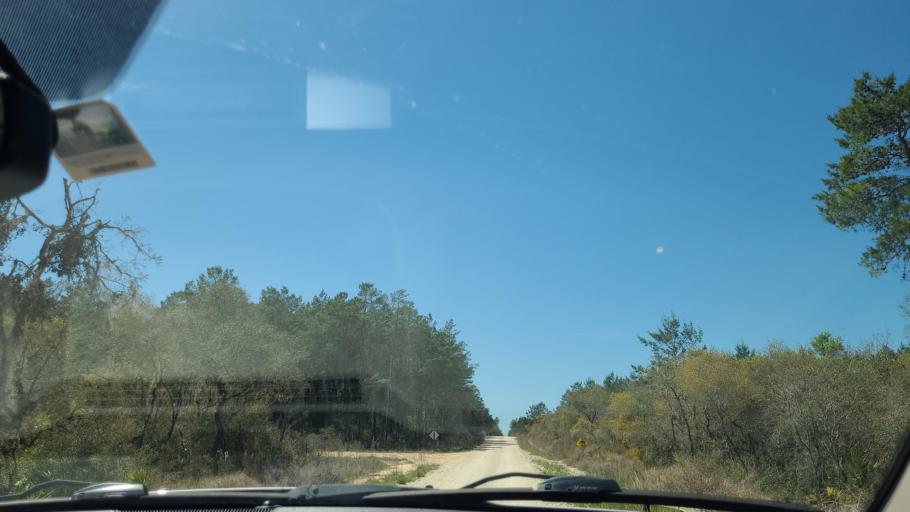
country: US
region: Florida
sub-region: Putnam County
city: Interlachen
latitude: 29.4287
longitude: -81.8241
